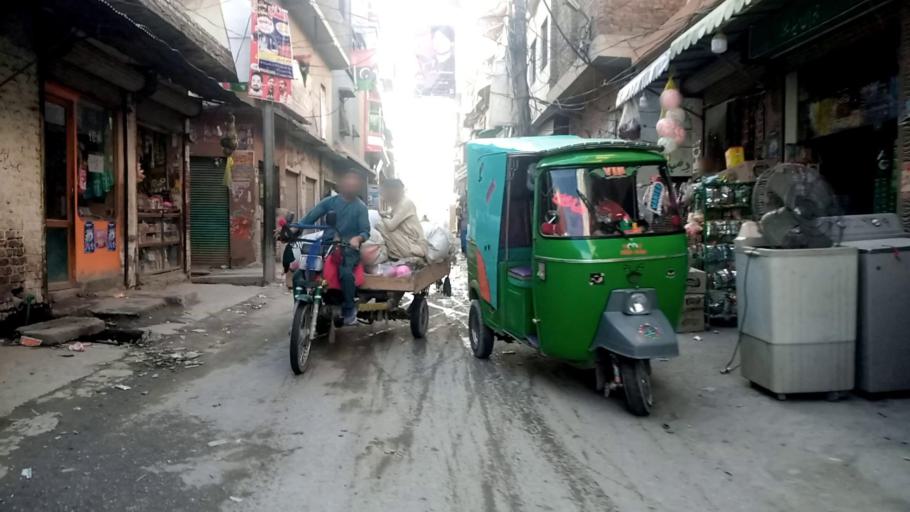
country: PK
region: Khyber Pakhtunkhwa
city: Peshawar
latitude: 34.0065
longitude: 71.5975
